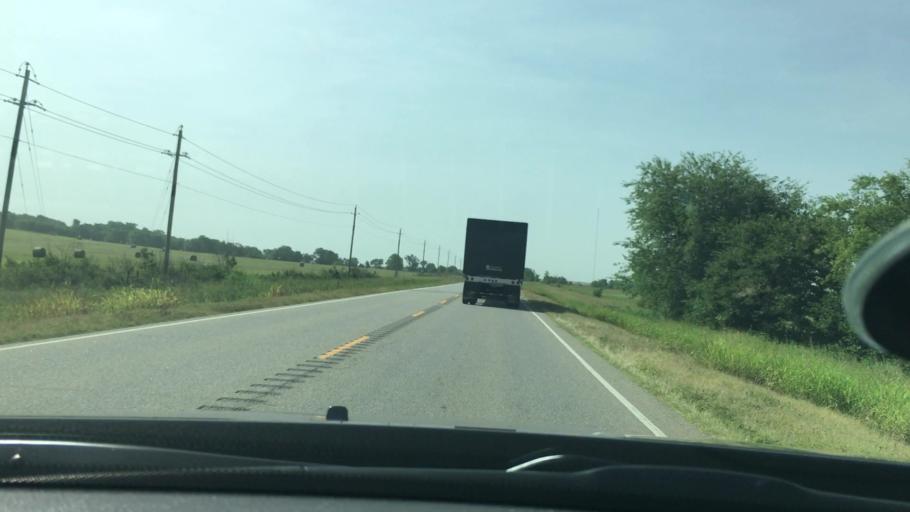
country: US
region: Oklahoma
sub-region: Atoka County
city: Atoka
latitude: 34.4313
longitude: -96.1977
